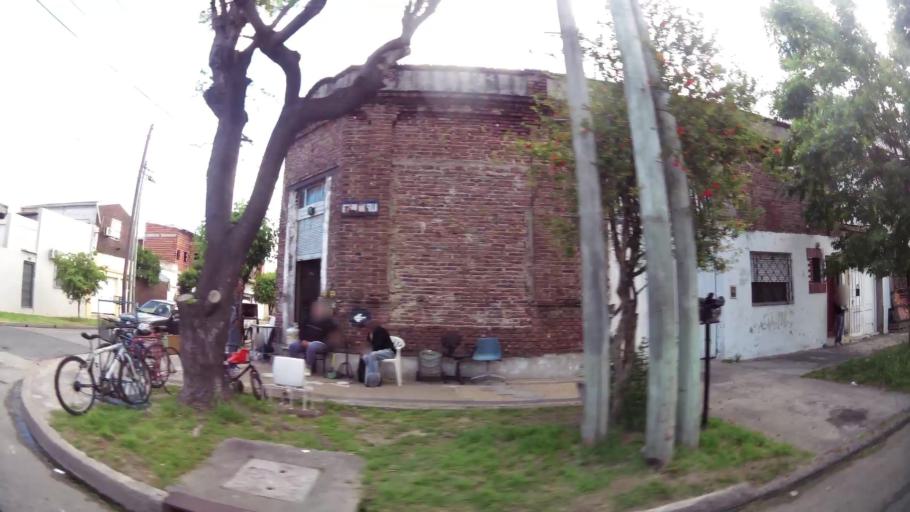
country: AR
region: Buenos Aires
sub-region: Partido de Avellaneda
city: Avellaneda
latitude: -34.6868
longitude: -58.3544
